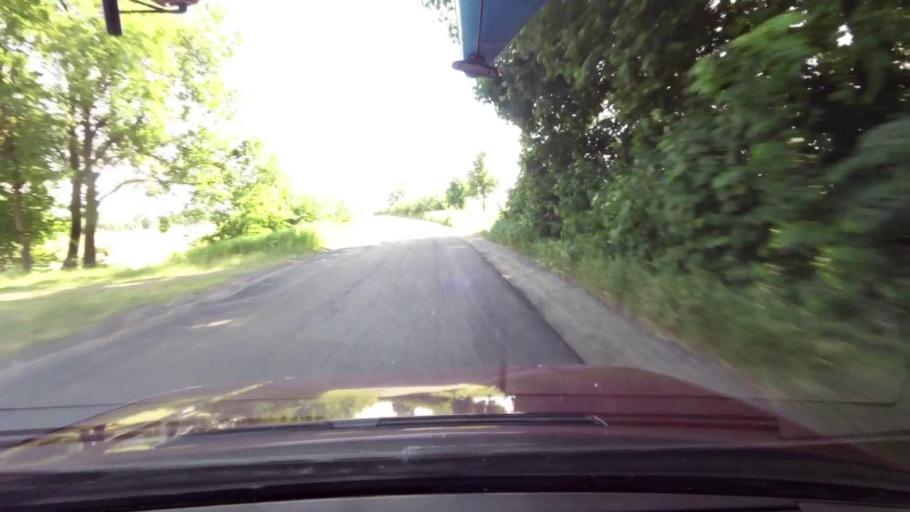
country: PL
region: Pomeranian Voivodeship
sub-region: Powiat slupski
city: Kobylnica
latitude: 54.3661
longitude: 16.9665
